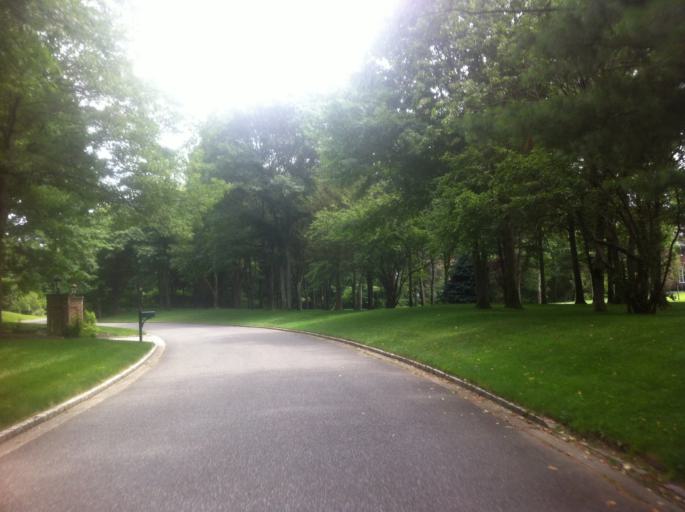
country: US
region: New York
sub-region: Nassau County
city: Upper Brookville
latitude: 40.8414
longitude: -73.5638
